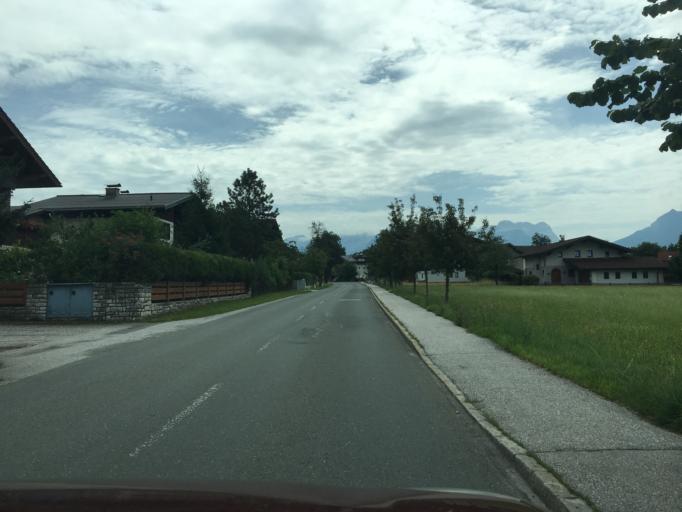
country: AT
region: Salzburg
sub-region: Politischer Bezirk Hallein
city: Adnet
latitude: 47.6626
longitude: 13.1397
